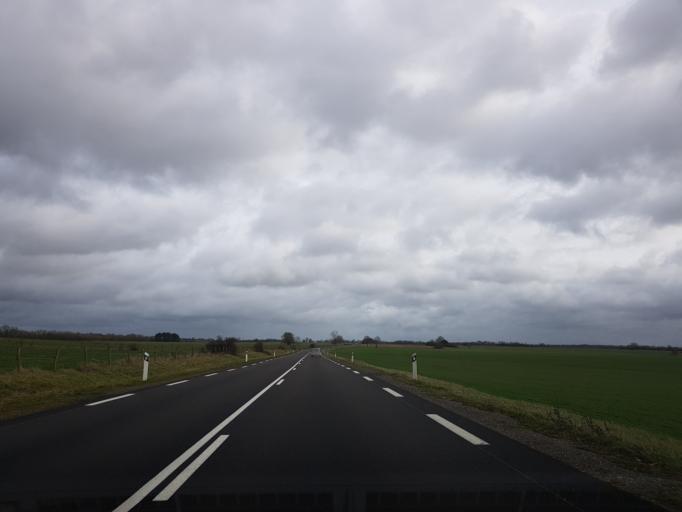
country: FR
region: Champagne-Ardenne
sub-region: Departement de la Haute-Marne
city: Chalindrey
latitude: 47.8486
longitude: 5.4222
